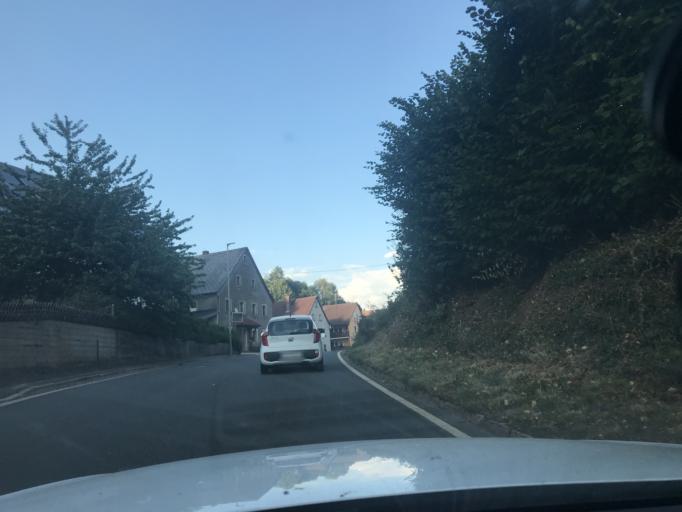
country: DE
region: Bavaria
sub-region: Upper Franconia
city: Obertrubach
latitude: 49.6940
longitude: 11.3880
